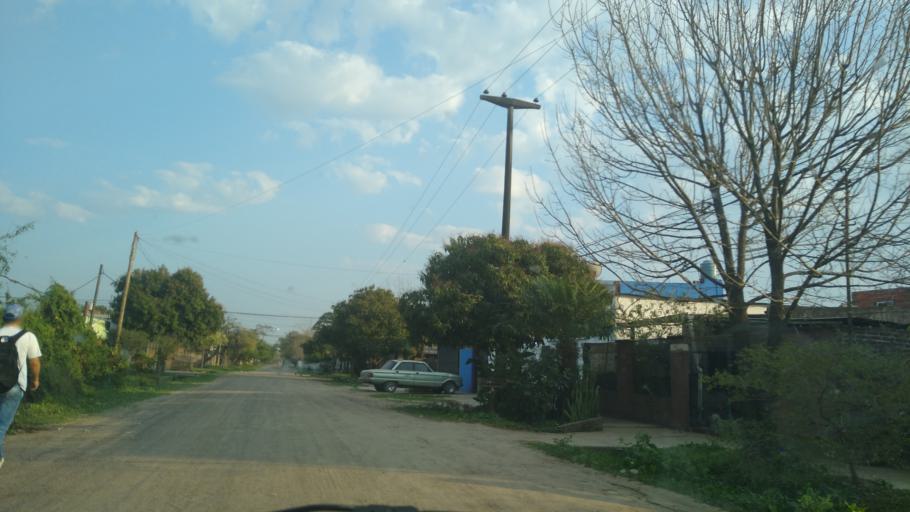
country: AR
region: Chaco
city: Resistencia
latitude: -27.4850
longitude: -58.9678
